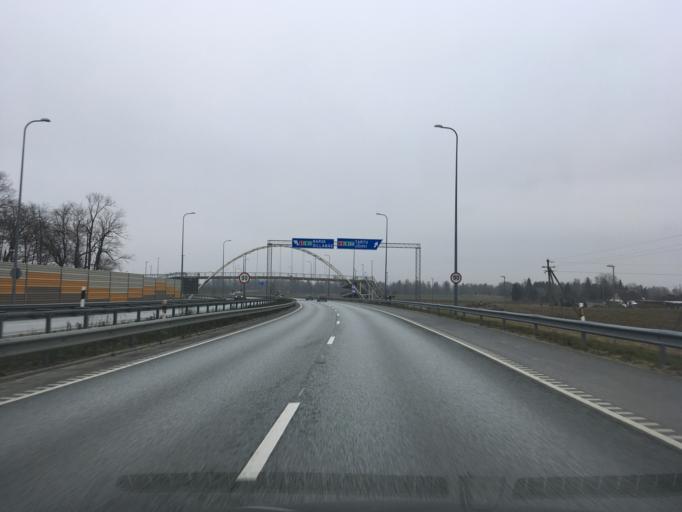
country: EE
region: Ida-Virumaa
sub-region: Johvi vald
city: Johvi
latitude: 59.3714
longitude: 27.3838
